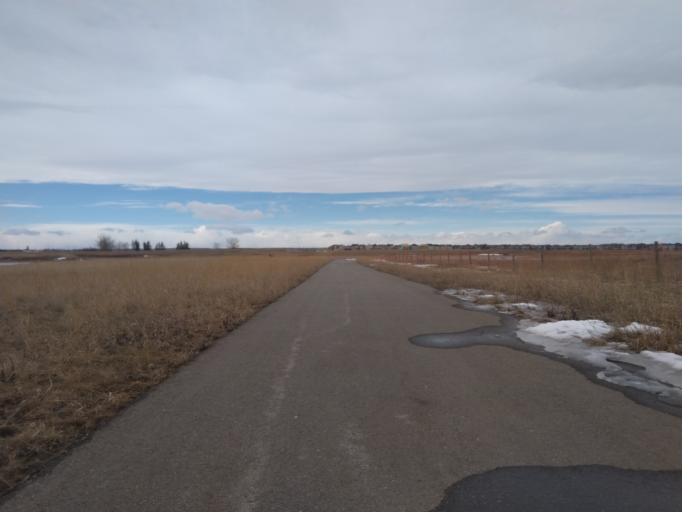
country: CA
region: Alberta
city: Calgary
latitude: 51.1434
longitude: -113.9488
